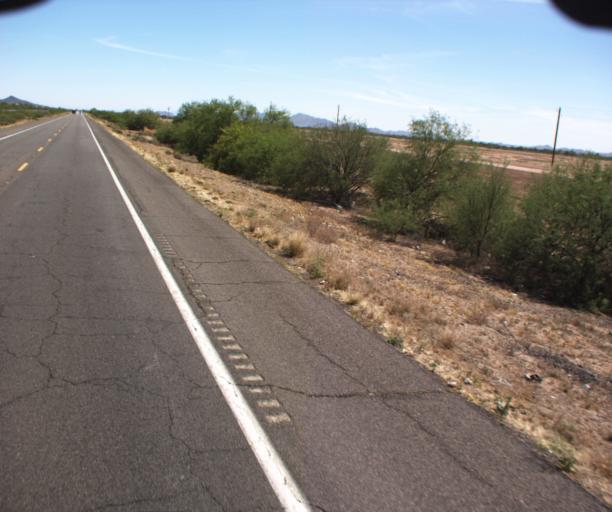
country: US
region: Arizona
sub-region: Maricopa County
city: Sun Lakes
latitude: 33.1657
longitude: -111.7877
